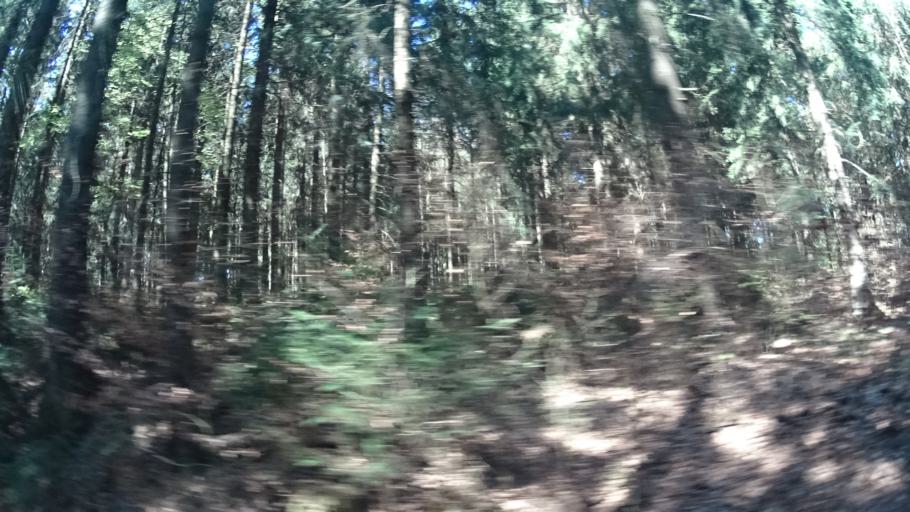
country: DE
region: Thuringia
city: Frauenwald
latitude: 50.5559
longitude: 10.8640
